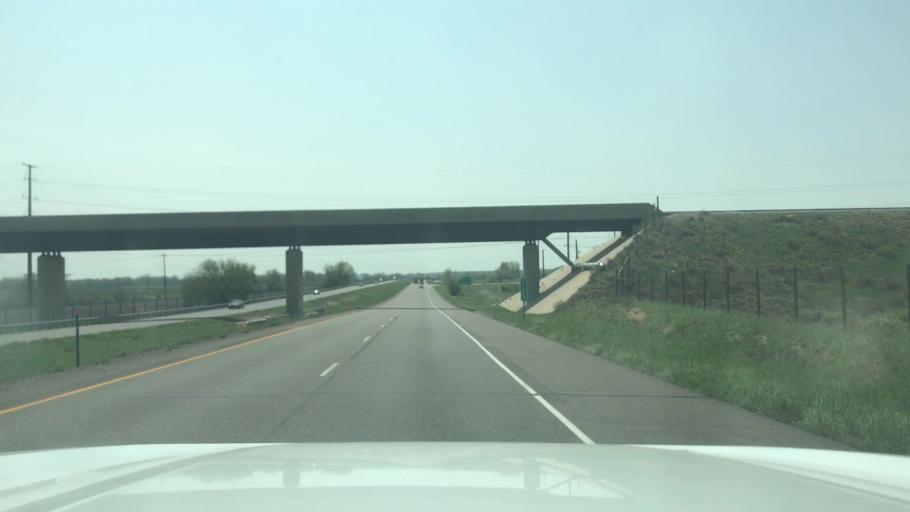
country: US
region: Colorado
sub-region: El Paso County
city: Fountain
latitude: 38.6342
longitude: -104.6921
